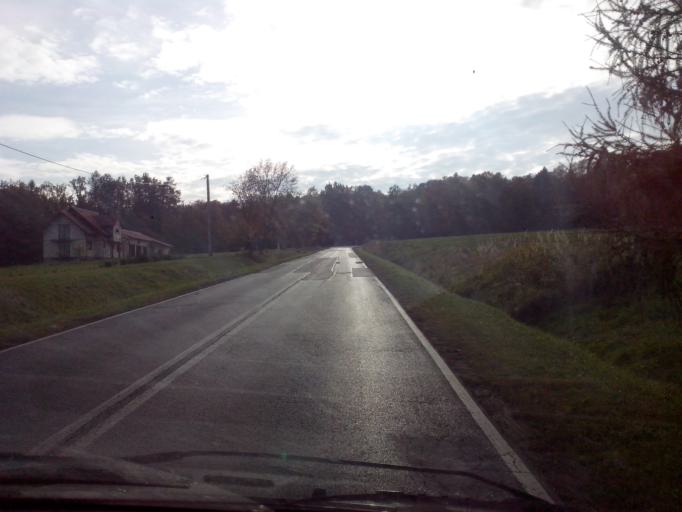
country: PL
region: Subcarpathian Voivodeship
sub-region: Powiat ropczycko-sedziszowski
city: Wielopole Skrzynskie
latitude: 49.9354
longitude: 21.6153
